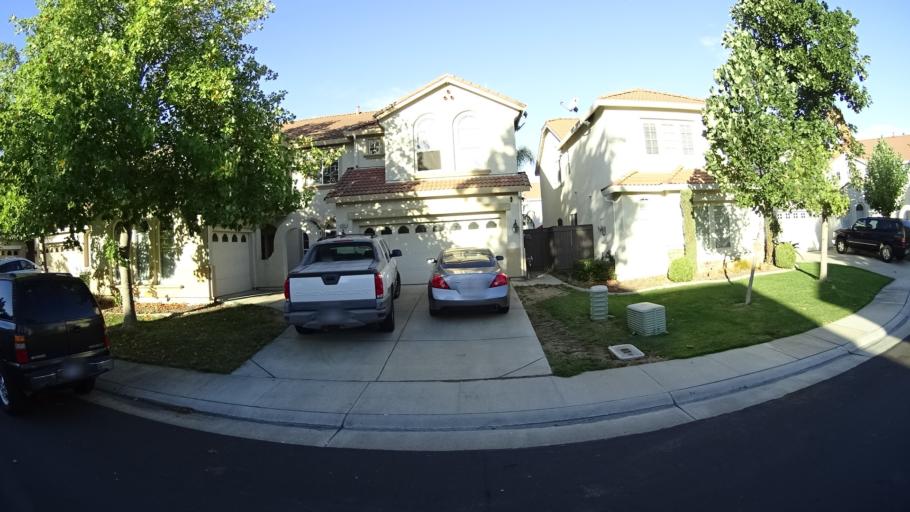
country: US
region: California
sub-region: Sacramento County
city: Laguna
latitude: 38.3963
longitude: -121.4781
